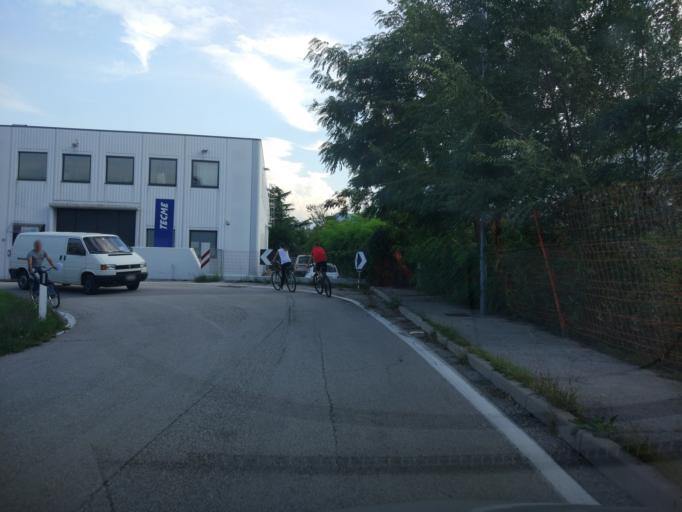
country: IT
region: Trentino-Alto Adige
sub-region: Provincia di Trento
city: Meano
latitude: 46.1165
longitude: 11.1009
